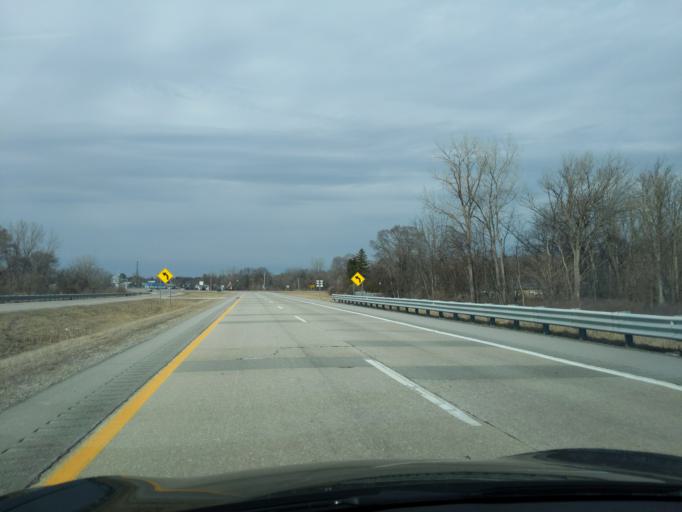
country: US
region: Michigan
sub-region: Bay County
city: Bay City
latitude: 43.6460
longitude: -83.9413
